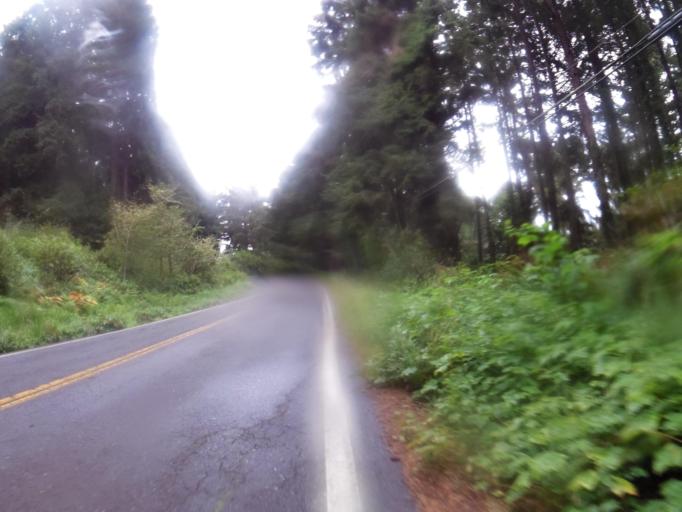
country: US
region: California
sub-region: Humboldt County
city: Westhaven-Moonstone
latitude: 41.1183
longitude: -124.1568
